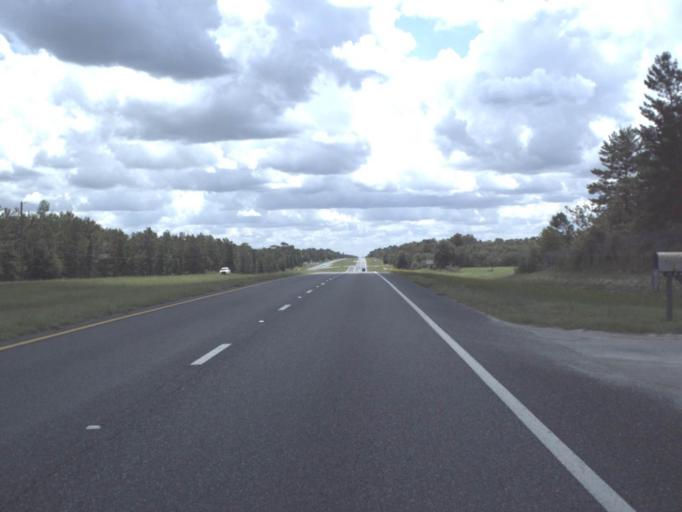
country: US
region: Florida
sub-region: Levy County
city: East Bronson
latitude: 29.4165
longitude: -82.5596
